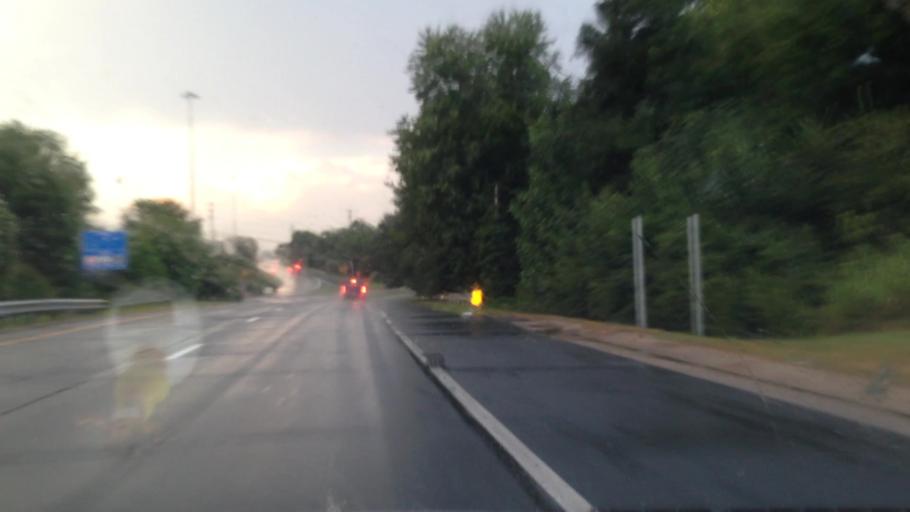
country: US
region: North Carolina
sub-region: Mecklenburg County
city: Pineville
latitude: 35.1363
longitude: -80.9084
